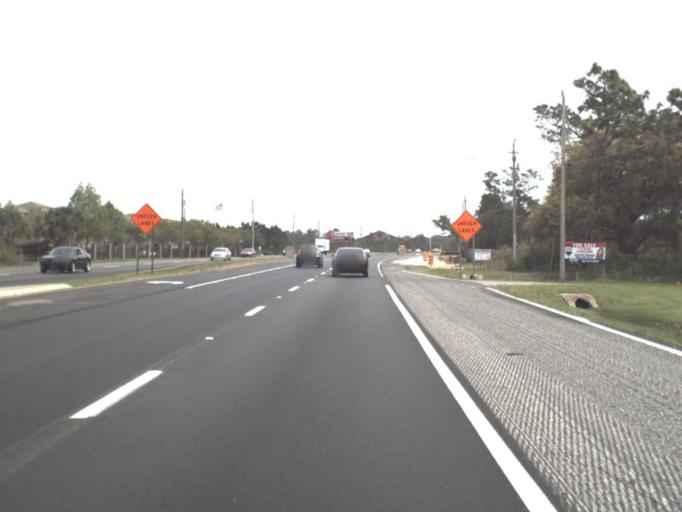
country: US
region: Florida
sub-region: Santa Rosa County
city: Woodlawn Beach
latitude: 30.4037
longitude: -86.9594
